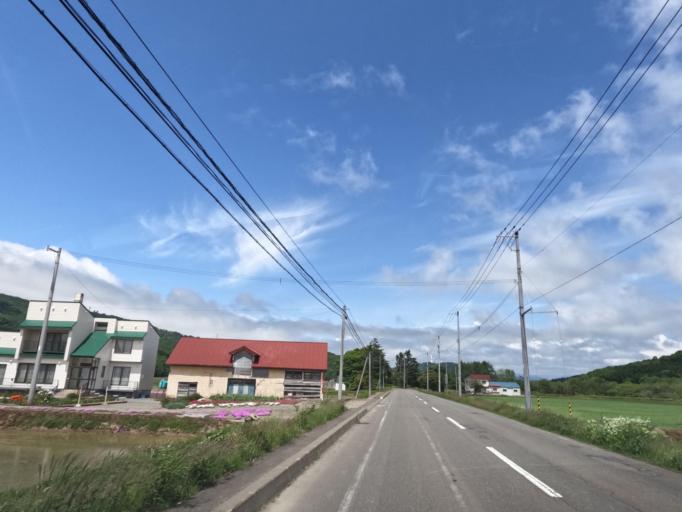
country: JP
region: Hokkaido
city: Tobetsu
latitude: 43.2858
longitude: 141.5374
